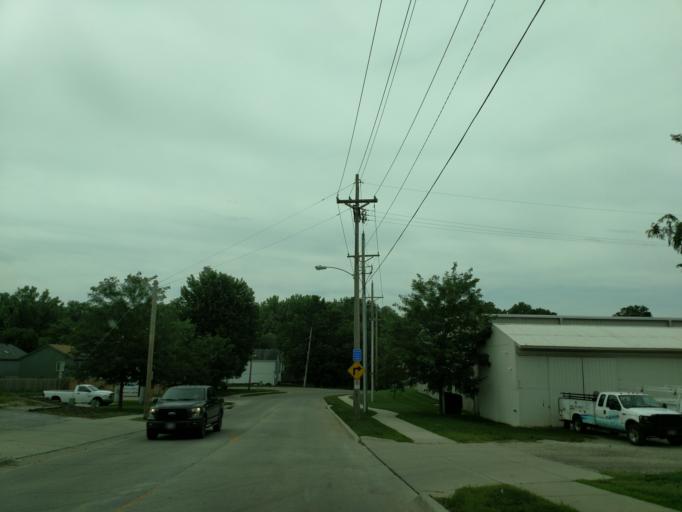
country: US
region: Nebraska
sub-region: Douglas County
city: Ralston
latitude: 41.1989
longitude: -96.0320
